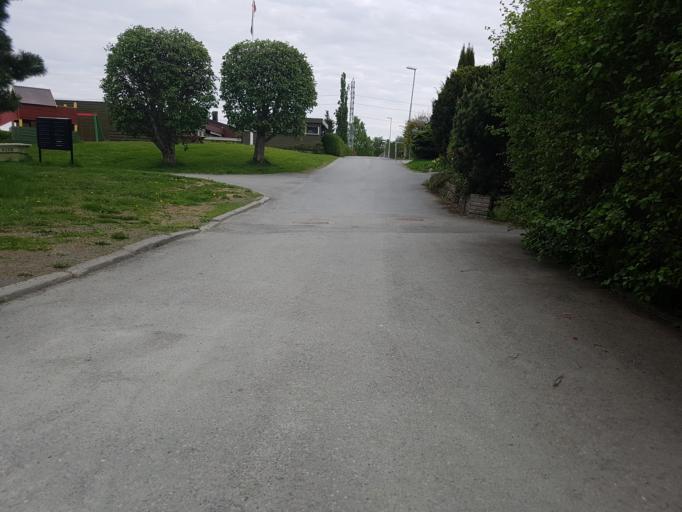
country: NO
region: Sor-Trondelag
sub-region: Trondheim
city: Trondheim
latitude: 63.4257
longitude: 10.4487
